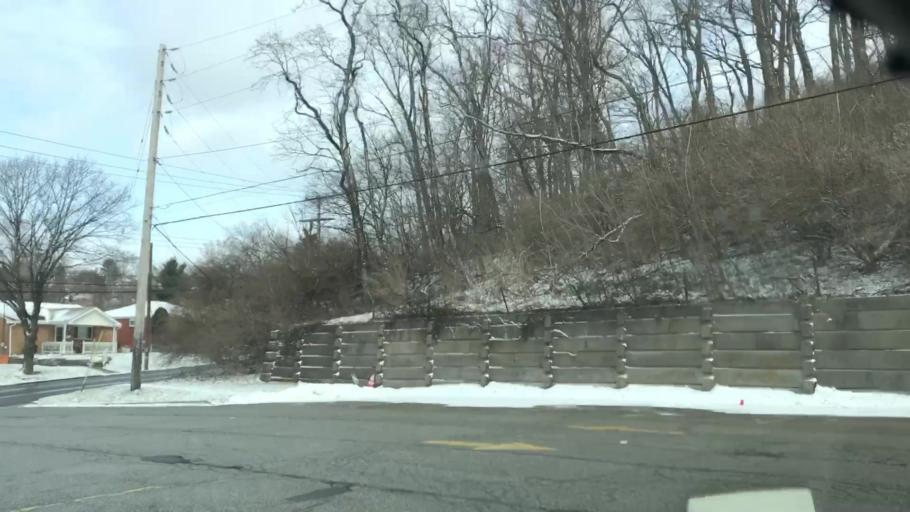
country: US
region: Pennsylvania
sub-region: Allegheny County
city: Crafton
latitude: 40.4317
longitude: -80.0524
